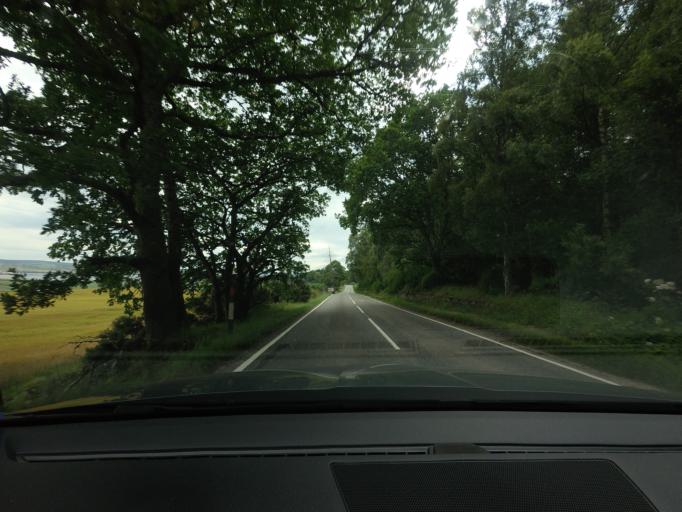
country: GB
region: Scotland
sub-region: Highland
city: Alness
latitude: 57.6963
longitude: -4.2894
